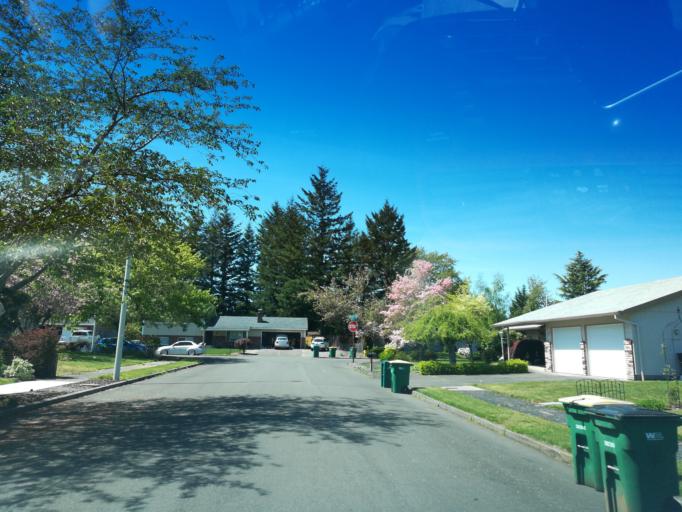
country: US
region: Oregon
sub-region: Multnomah County
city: Troutdale
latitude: 45.5267
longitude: -122.3945
